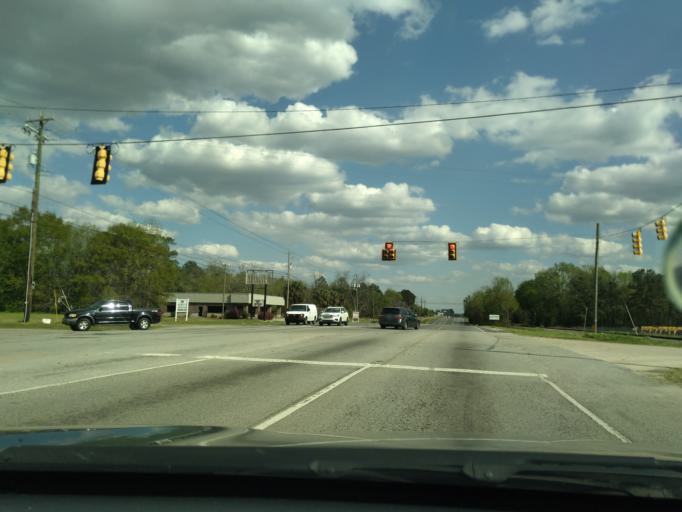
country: US
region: South Carolina
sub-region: Florence County
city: Florence
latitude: 34.2221
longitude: -79.7900
